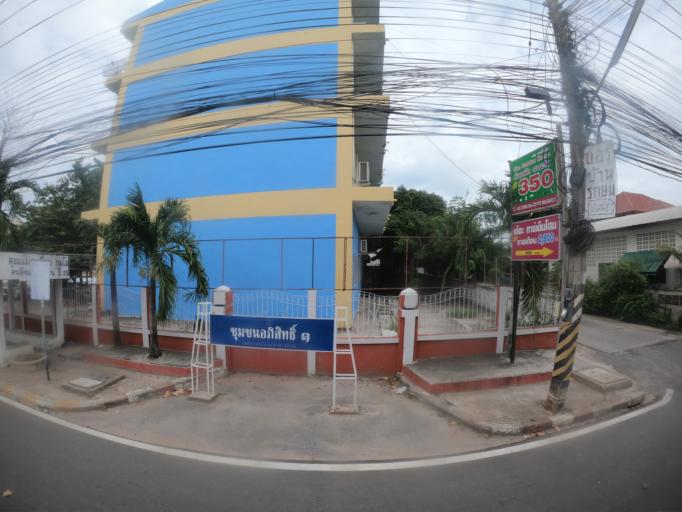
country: TH
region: Maha Sarakham
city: Maha Sarakham
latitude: 16.1787
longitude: 103.3103
